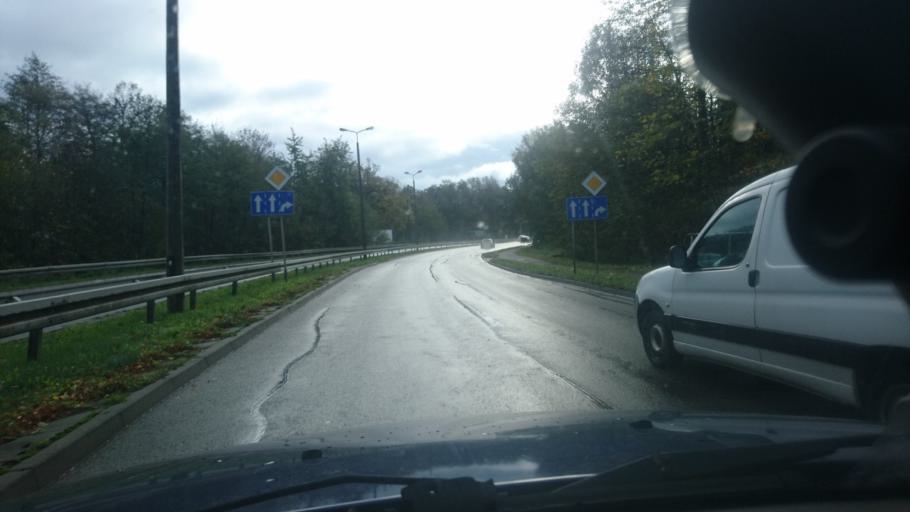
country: PL
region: Silesian Voivodeship
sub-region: Powiat bielski
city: Mazancowice
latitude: 49.8375
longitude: 19.0077
